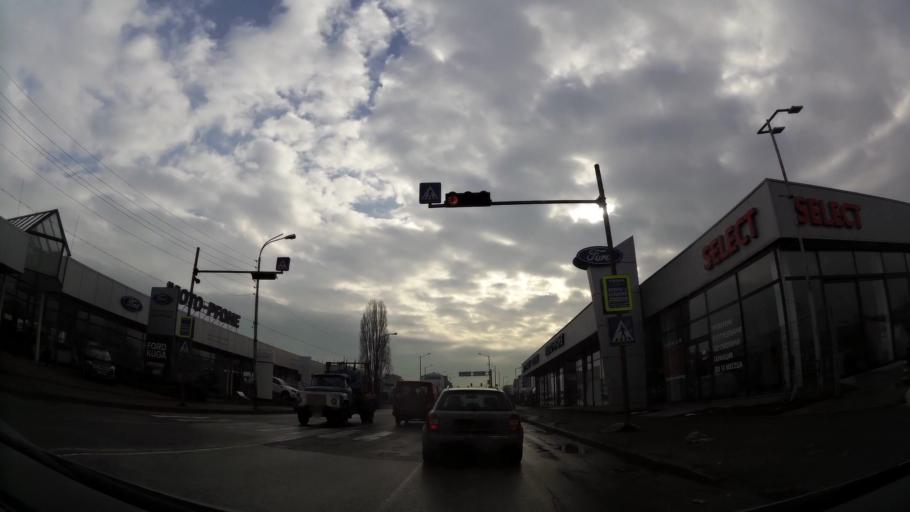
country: BG
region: Sofiya
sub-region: Obshtina Bozhurishte
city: Bozhurishte
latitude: 42.7279
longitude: 23.2598
